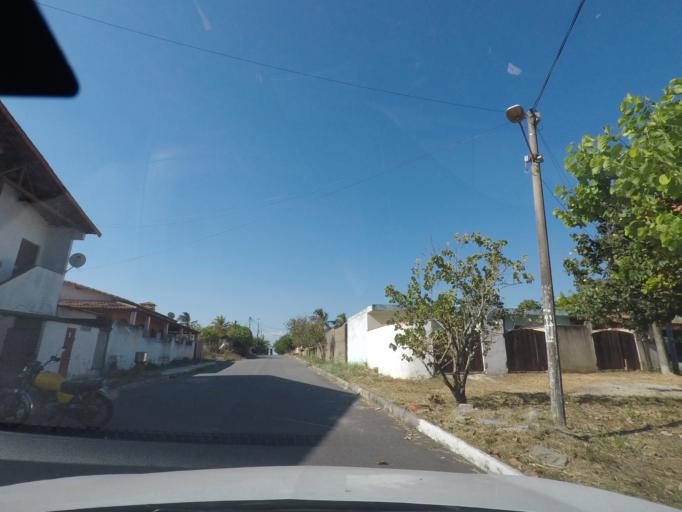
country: BR
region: Rio de Janeiro
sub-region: Marica
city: Marica
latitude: -22.9714
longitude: -42.9199
